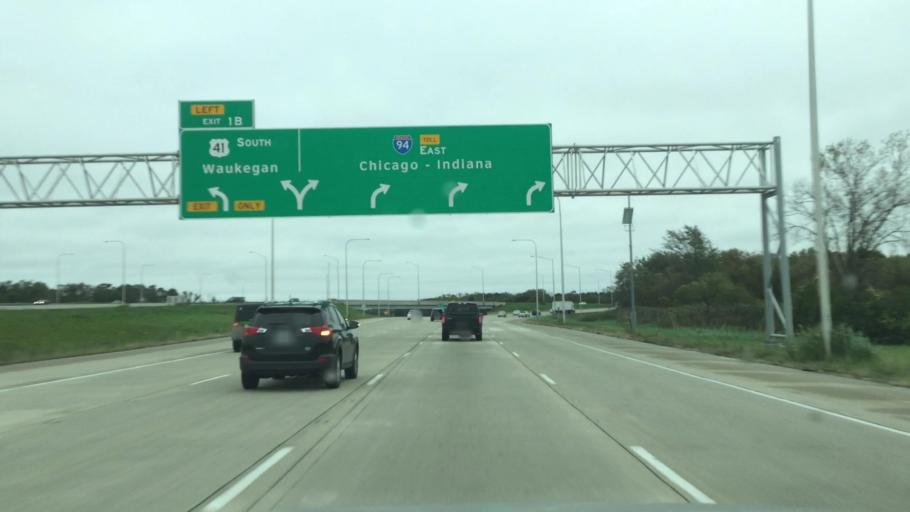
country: US
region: Illinois
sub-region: Lake County
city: Wadsworth
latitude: 42.4826
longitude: -87.9476
